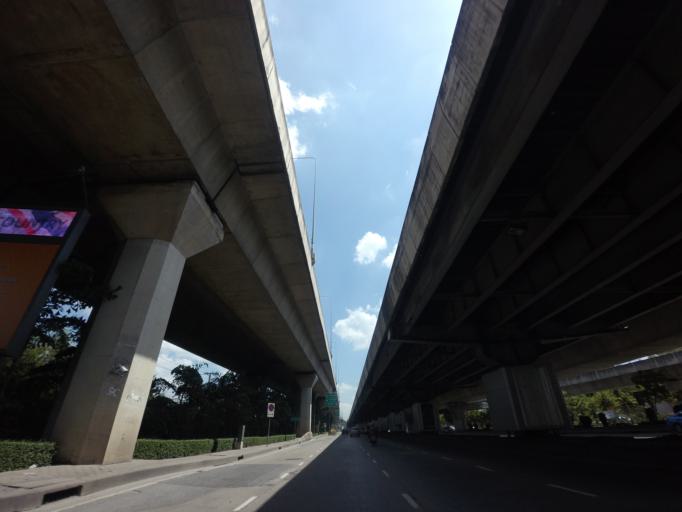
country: TH
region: Bangkok
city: Watthana
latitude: 13.7502
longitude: 100.5976
